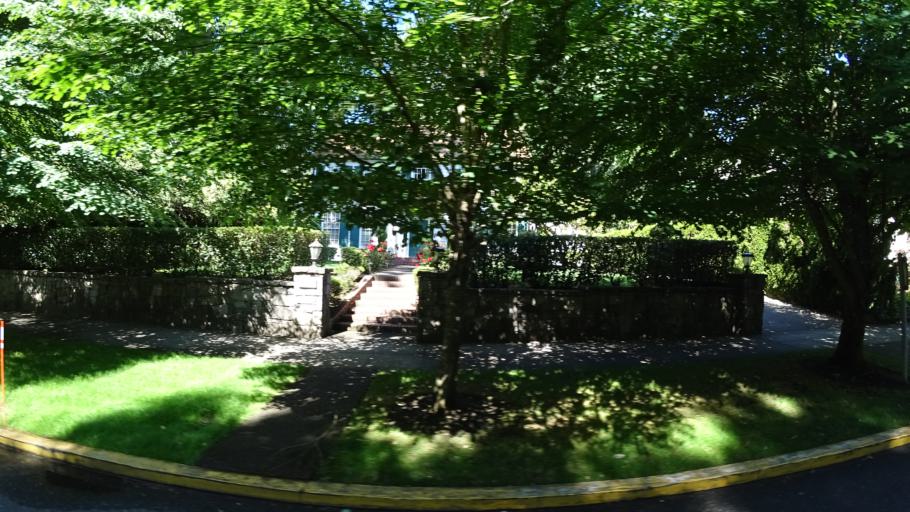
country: US
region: Oregon
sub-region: Multnomah County
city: Portland
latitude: 45.5209
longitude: -122.7068
